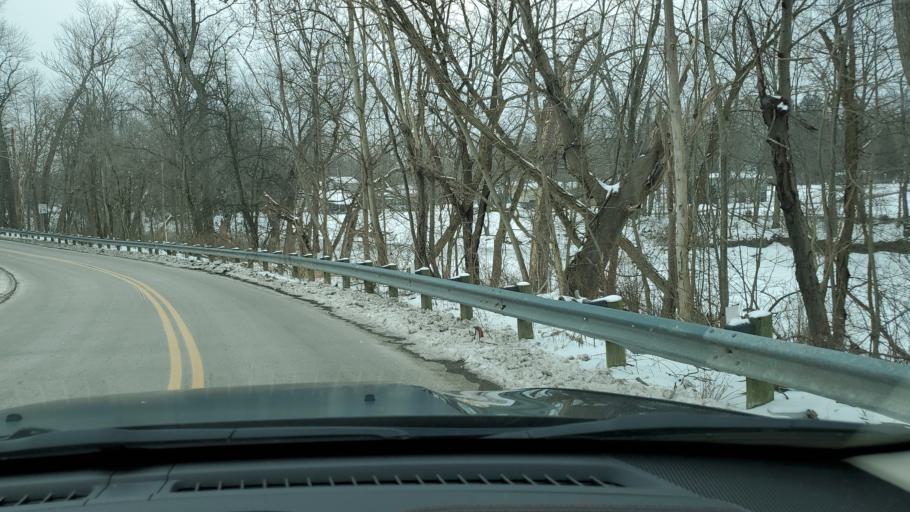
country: US
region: Ohio
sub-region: Trumbull County
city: Leavittsburg
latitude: 41.2569
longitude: -80.8641
